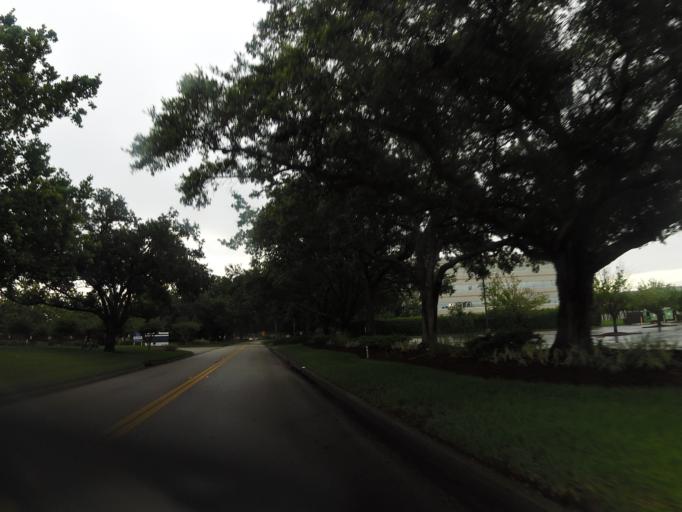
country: US
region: Florida
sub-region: Duval County
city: Jacksonville
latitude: 30.2519
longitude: -81.5901
